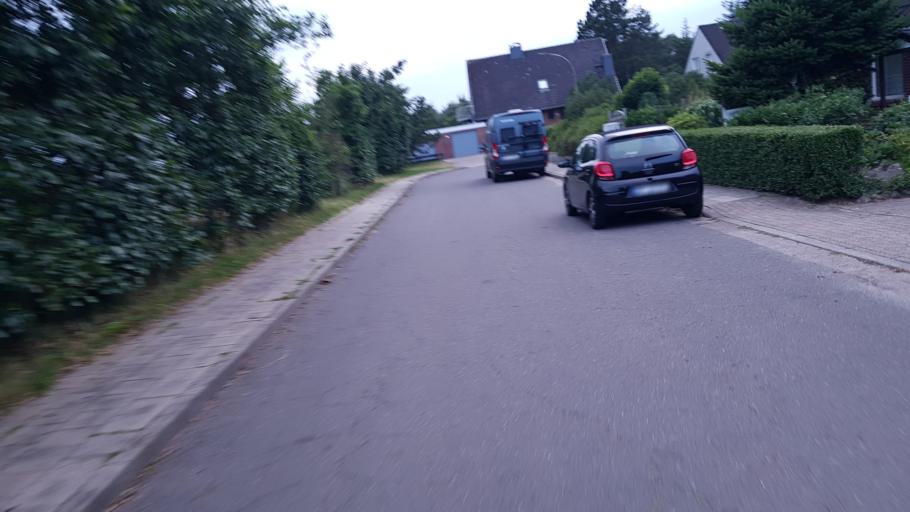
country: DE
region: Schleswig-Holstein
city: Sankt Peter-Ording
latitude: 54.3034
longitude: 8.6312
